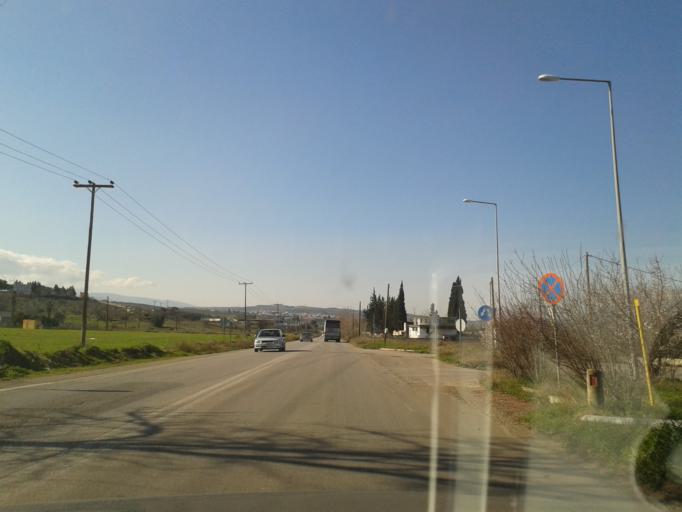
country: GR
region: Central Greece
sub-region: Nomos Voiotias
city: Thivai
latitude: 38.3417
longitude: 23.3565
